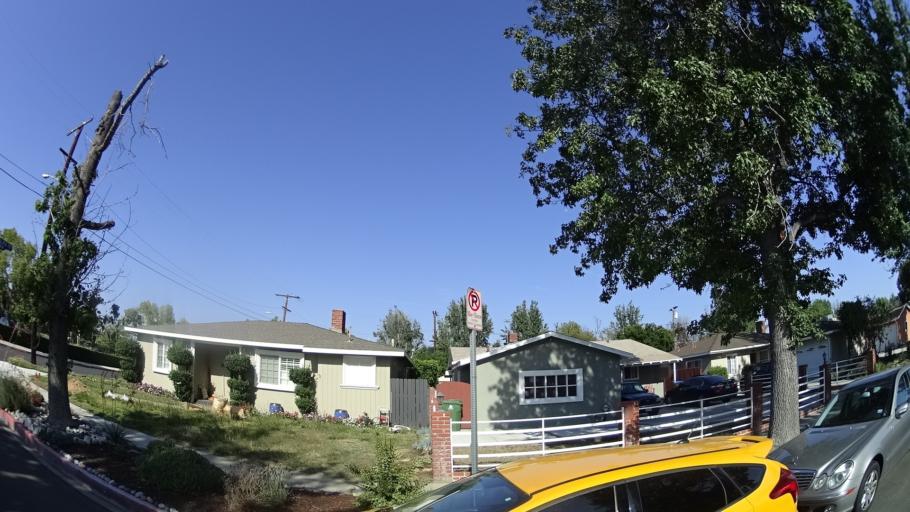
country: US
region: California
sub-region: Los Angeles County
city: Van Nuys
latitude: 34.1774
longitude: -118.4564
